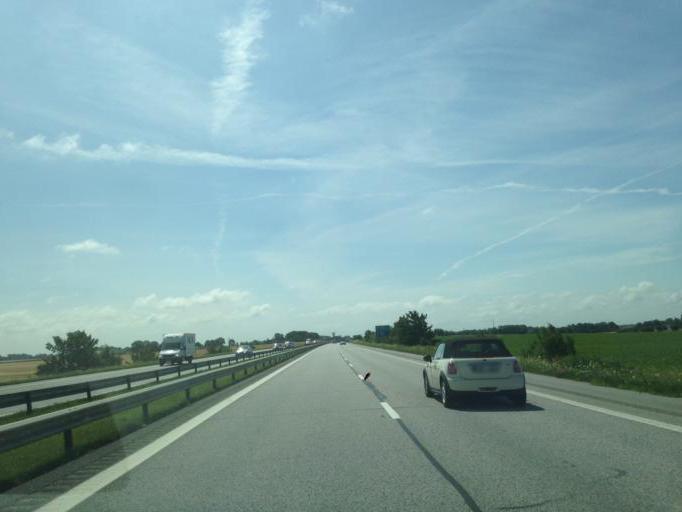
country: SE
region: Skane
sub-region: Vellinge Kommun
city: Vellinge
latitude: 55.4971
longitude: 13.0200
